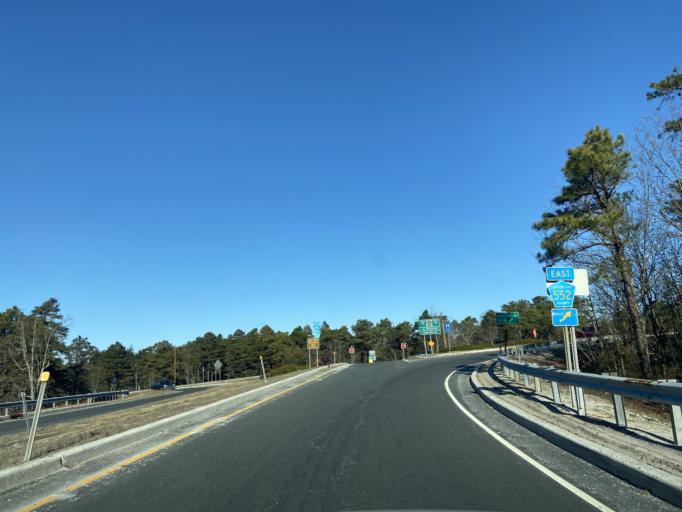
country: US
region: New Jersey
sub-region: Cumberland County
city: South Vineland
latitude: 39.4470
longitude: -75.0656
